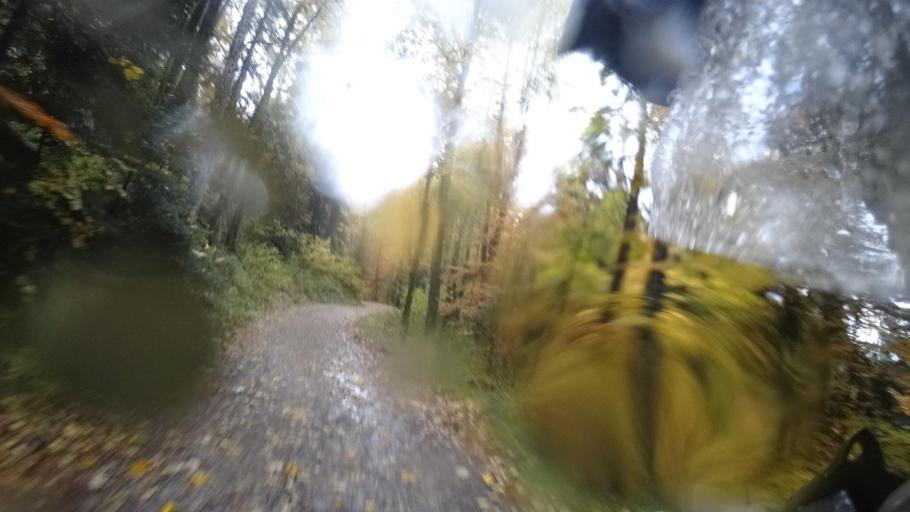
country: HR
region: Primorsko-Goranska
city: Vrbovsko
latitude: 45.3116
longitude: 15.0749
